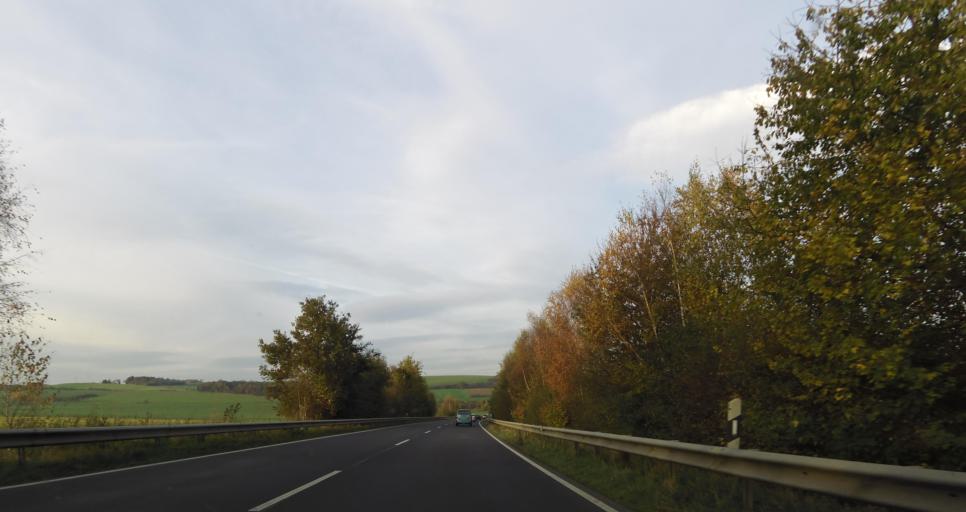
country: DE
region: Lower Saxony
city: Einbeck
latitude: 51.8294
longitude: 9.8305
